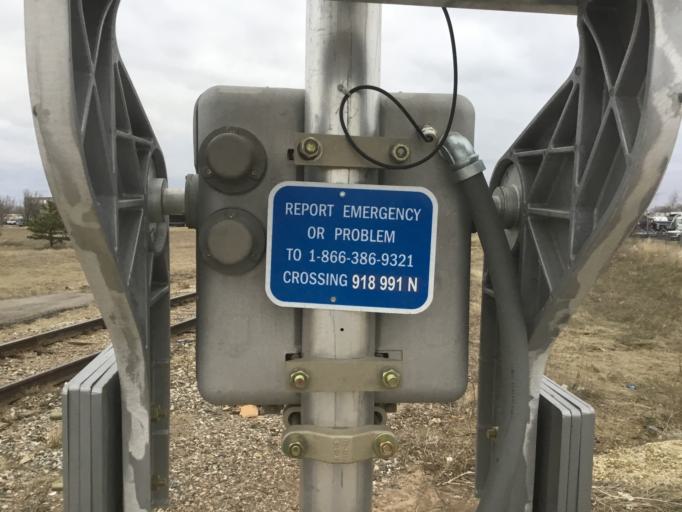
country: US
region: Kansas
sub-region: Sedgwick County
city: Wichita
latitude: 37.6404
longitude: -97.3919
